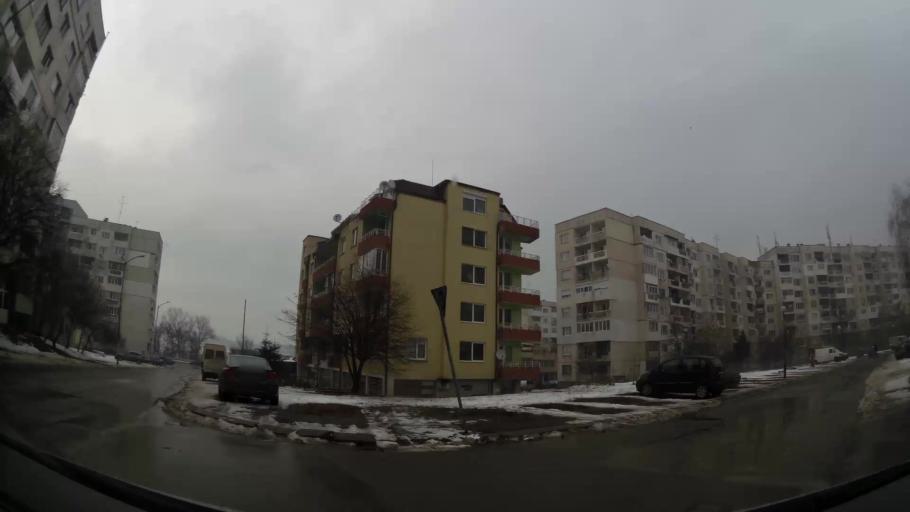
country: BG
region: Sofiya
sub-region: Obshtina Bozhurishte
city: Bozhurishte
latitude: 42.6879
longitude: 23.2443
